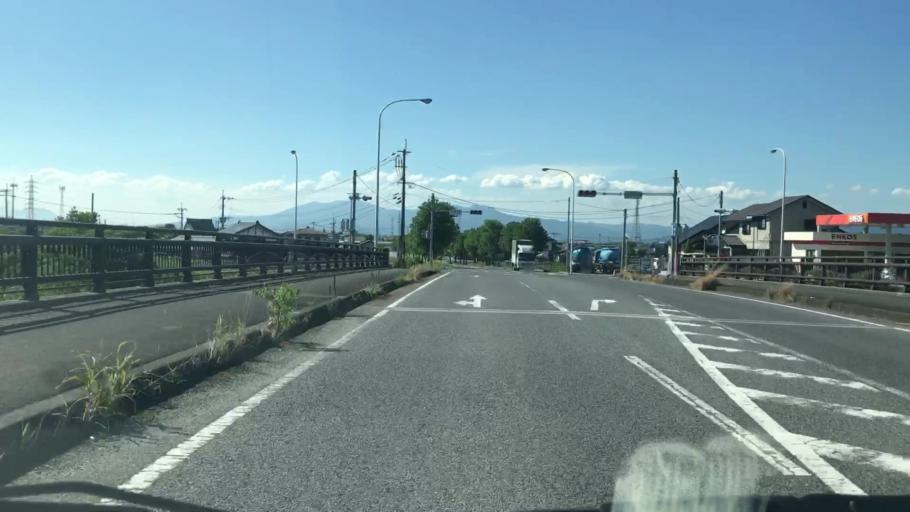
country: JP
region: Saga Prefecture
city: Okawa
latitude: 33.2283
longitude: 130.3702
